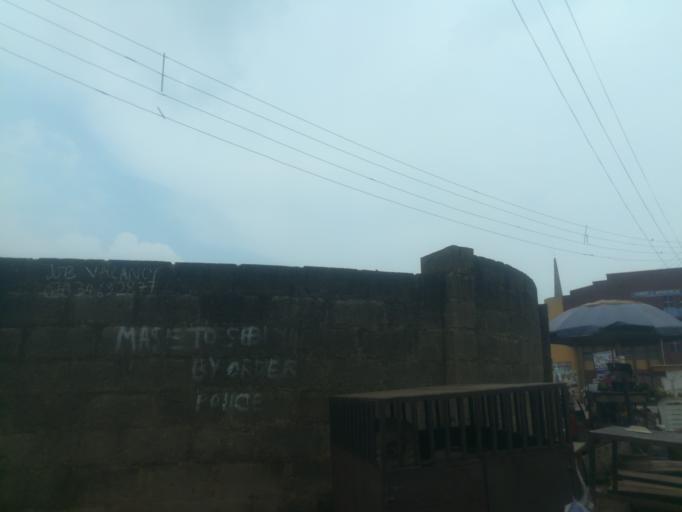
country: NG
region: Oyo
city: Ibadan
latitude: 7.4293
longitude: 3.9265
